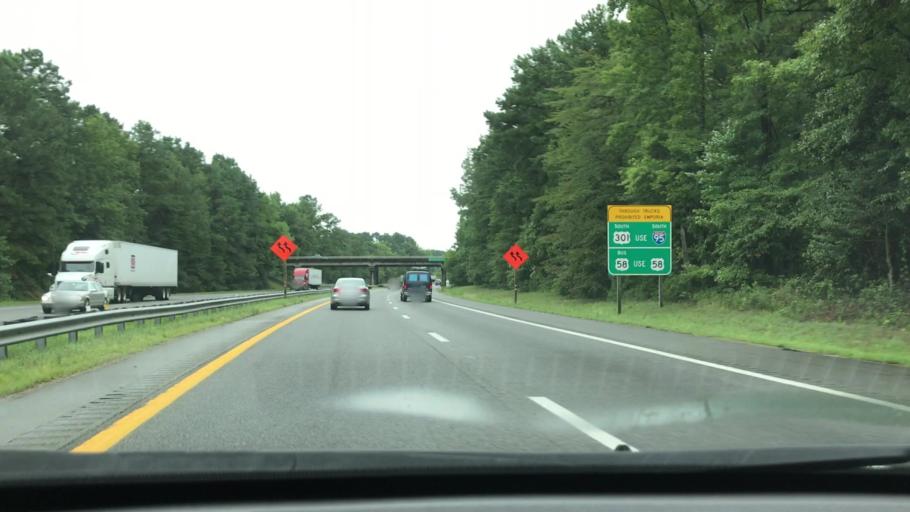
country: US
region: Virginia
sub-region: City of Emporia
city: Emporia
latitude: 36.6850
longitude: -77.5580
